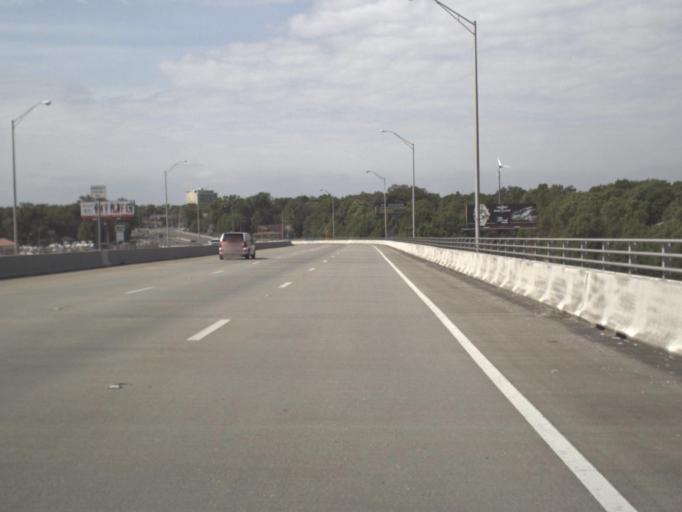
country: US
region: Florida
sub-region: Escambia County
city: Warrington
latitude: 30.4011
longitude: -87.2485
